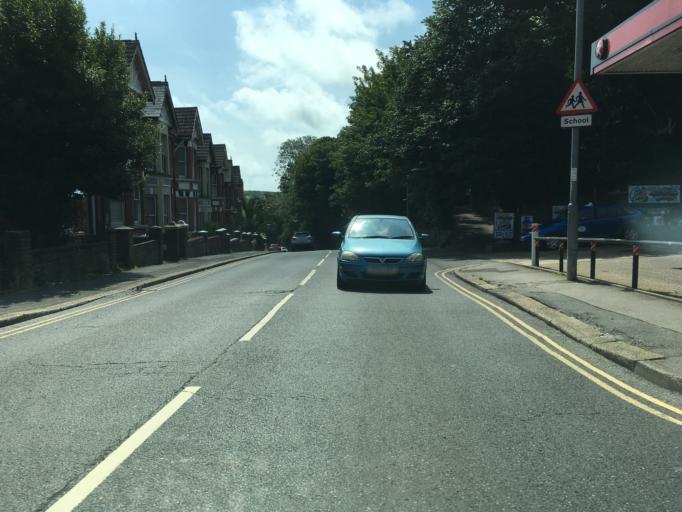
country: GB
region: England
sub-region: East Sussex
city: Hastings
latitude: 50.8652
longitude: 0.5976
